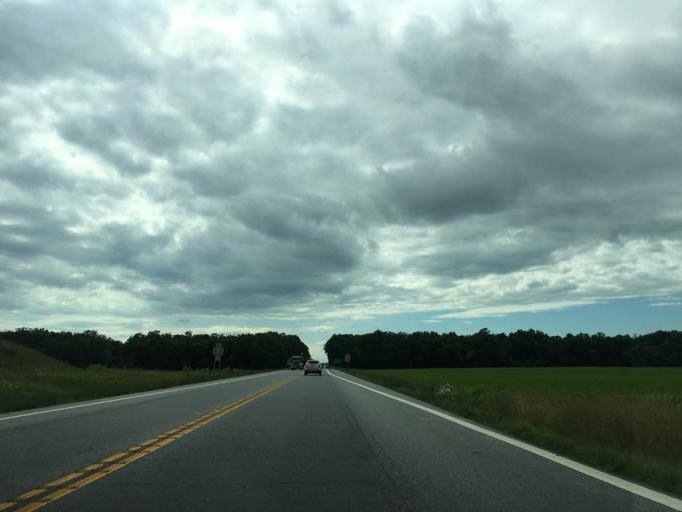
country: US
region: Maryland
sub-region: Caroline County
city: Ridgely
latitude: 38.9184
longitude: -75.9154
